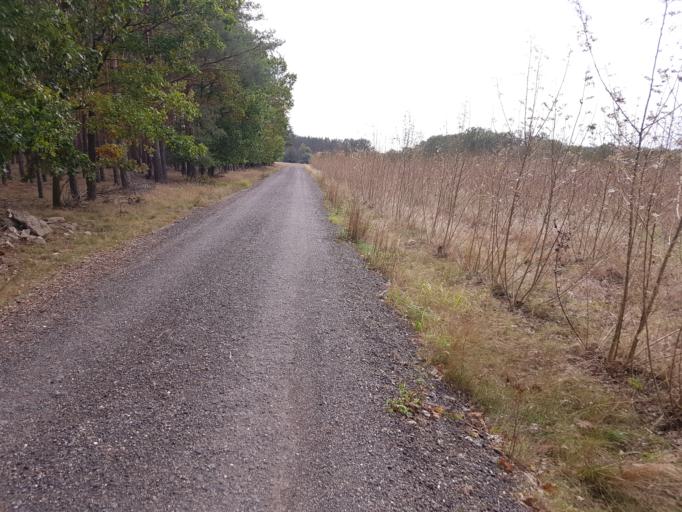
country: DE
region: Brandenburg
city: Bad Liebenwerda
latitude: 51.5428
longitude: 13.4019
